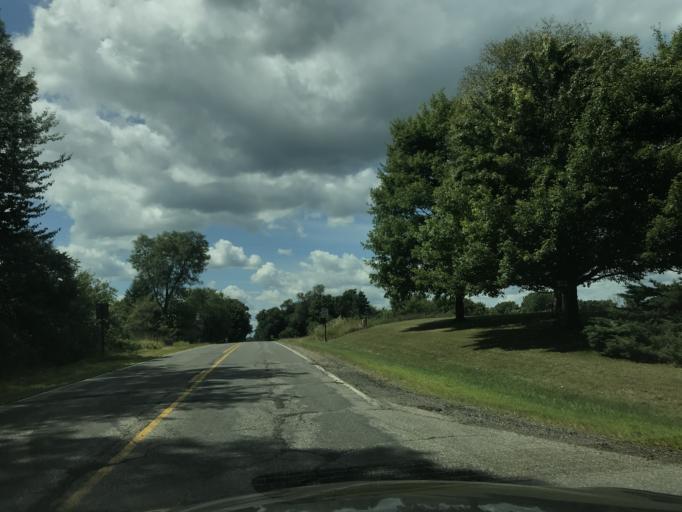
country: US
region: Michigan
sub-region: Ingham County
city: Leslie
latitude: 42.4510
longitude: -84.5460
